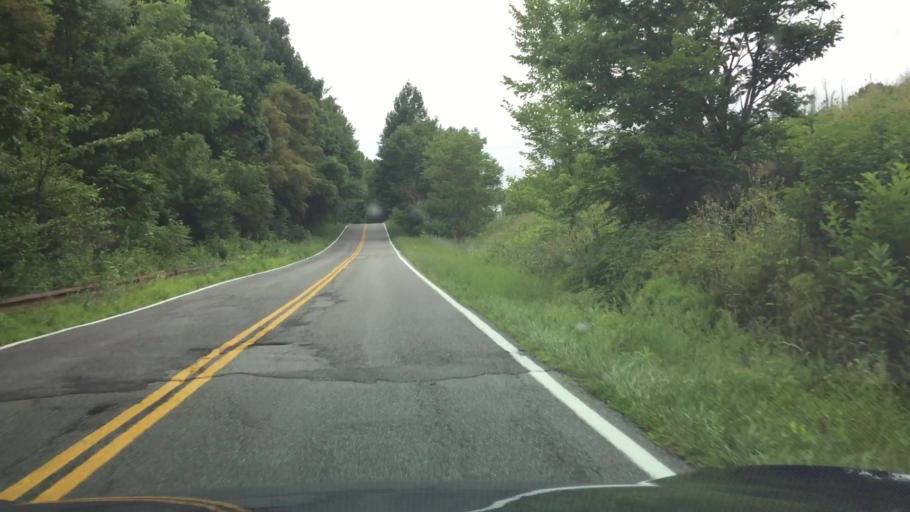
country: US
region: Virginia
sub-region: Pulaski County
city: Pulaski
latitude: 37.0121
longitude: -80.7405
